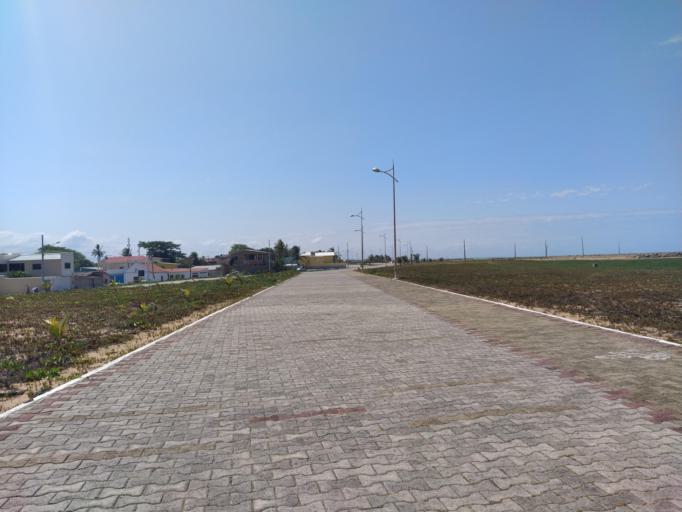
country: BR
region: Espirito Santo
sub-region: Conceicao Da Barra
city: Conceicao da Barra
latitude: -18.5992
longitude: -39.7281
